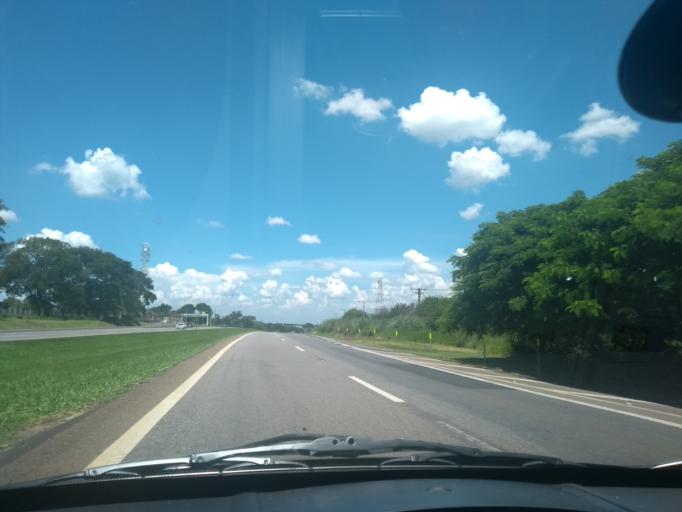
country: BR
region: Sao Paulo
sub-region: Mogi-Mirim
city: Mogi Mirim
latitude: -22.4891
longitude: -46.9814
